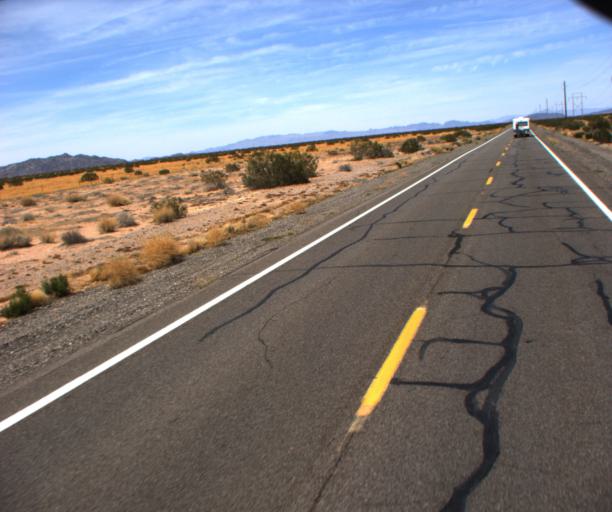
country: US
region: Arizona
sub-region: La Paz County
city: Parker
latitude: 33.9274
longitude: -114.2169
